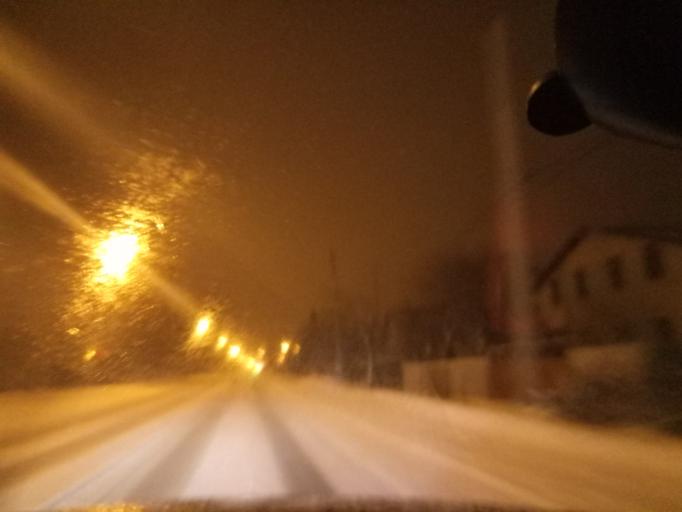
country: RU
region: Tula
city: Novomoskovsk
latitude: 54.0003
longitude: 38.2961
